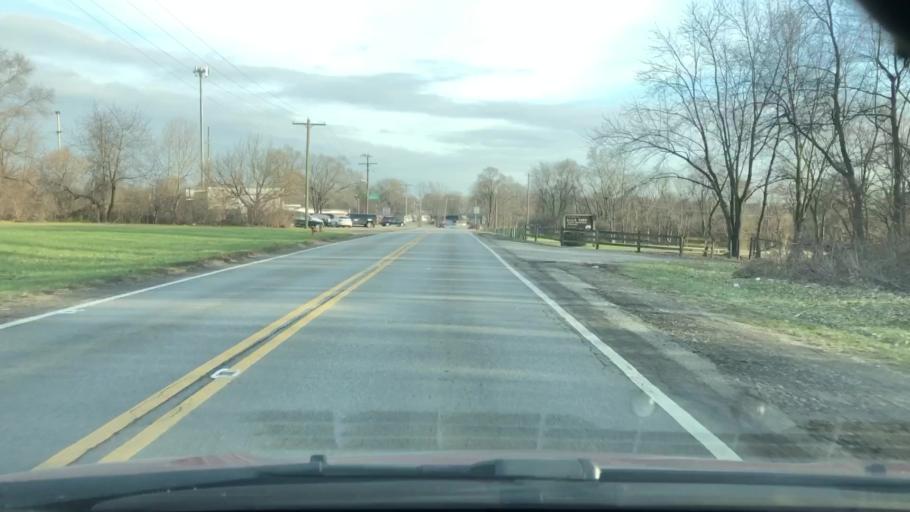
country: US
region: Ohio
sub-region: Franklin County
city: Obetz
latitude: 39.9064
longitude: -82.9709
